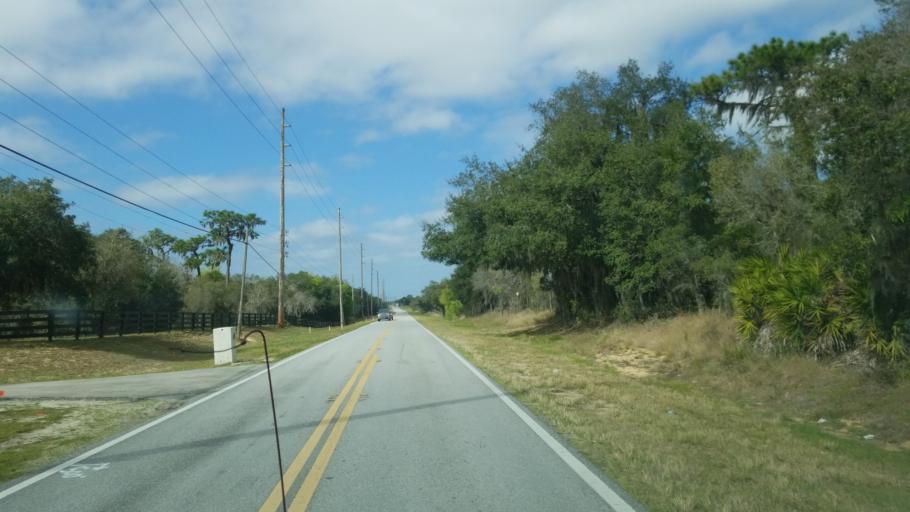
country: US
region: Florida
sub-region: Polk County
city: Lake Wales
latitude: 27.9615
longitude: -81.5412
